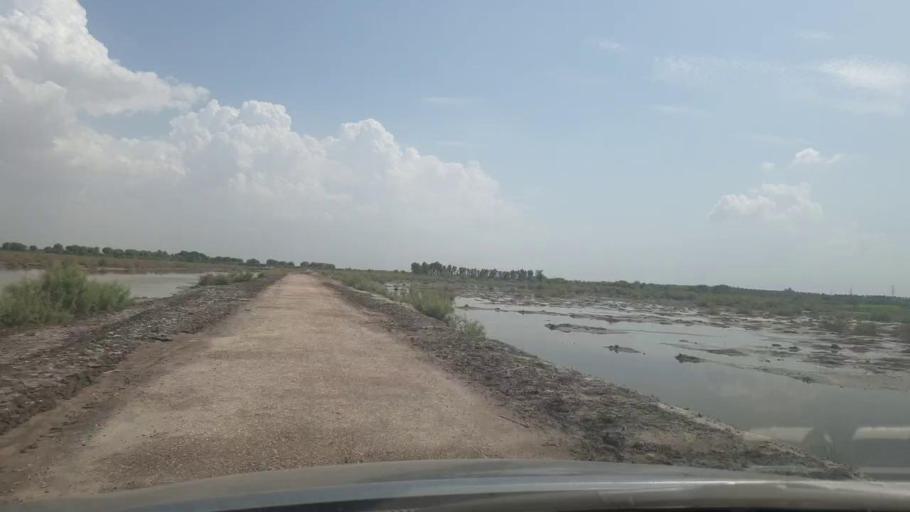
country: PK
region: Sindh
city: Khairpur
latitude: 27.5418
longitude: 68.8037
